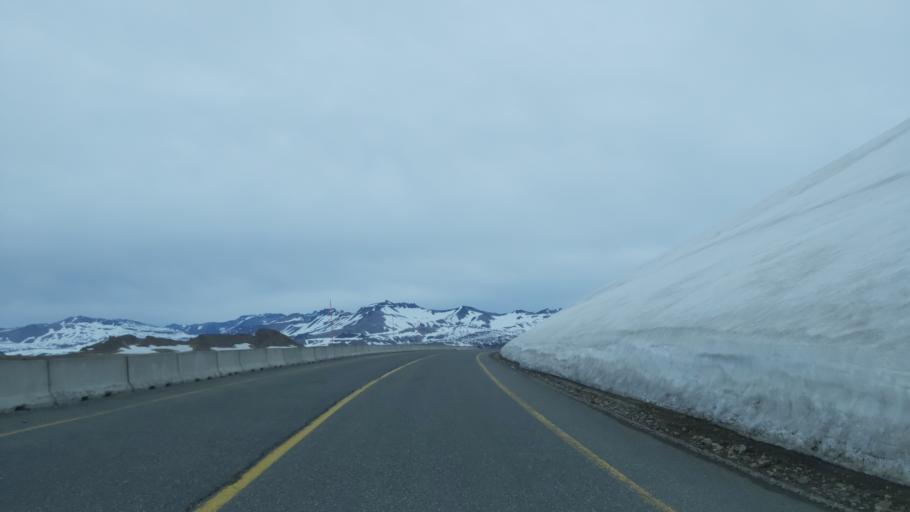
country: CL
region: Maule
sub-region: Provincia de Linares
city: Colbun
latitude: -36.0180
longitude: -70.4984
